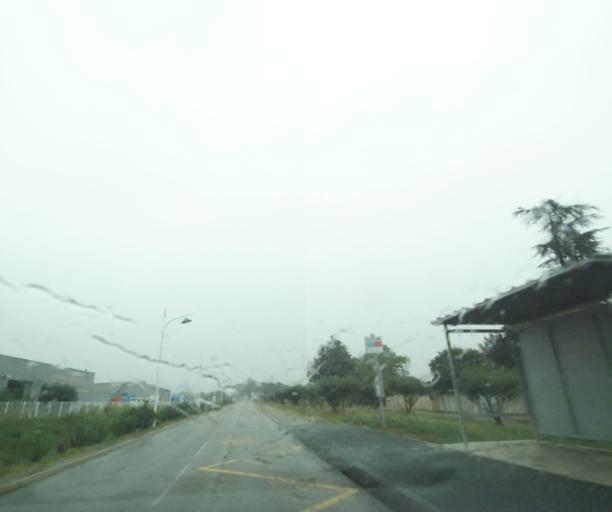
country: FR
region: Languedoc-Roussillon
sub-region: Departement du Gard
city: Milhaud
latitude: 43.7976
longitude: 4.3143
